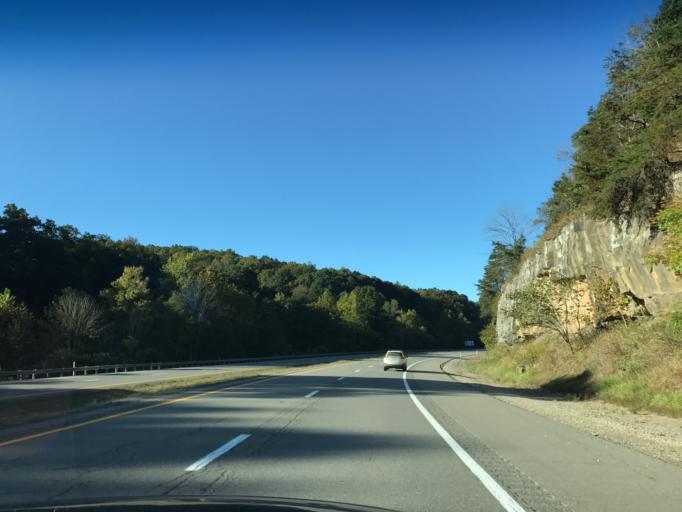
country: US
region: Ohio
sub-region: Washington County
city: Newport
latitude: 39.2552
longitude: -81.2958
